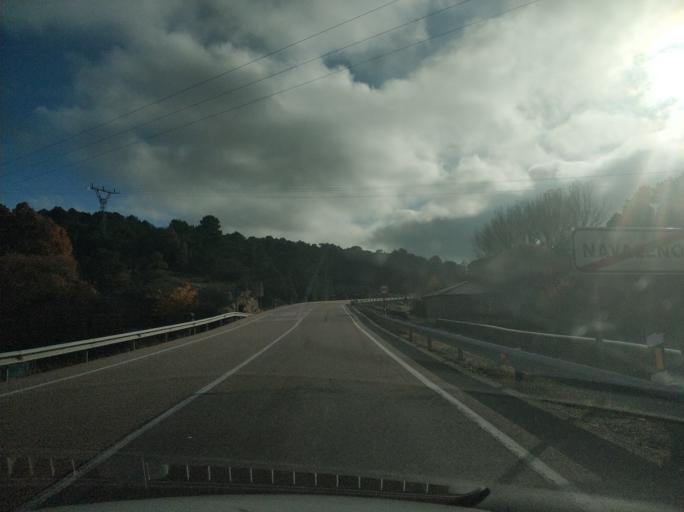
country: ES
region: Castille and Leon
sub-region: Provincia de Soria
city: Navaleno
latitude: 41.8360
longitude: -3.0024
